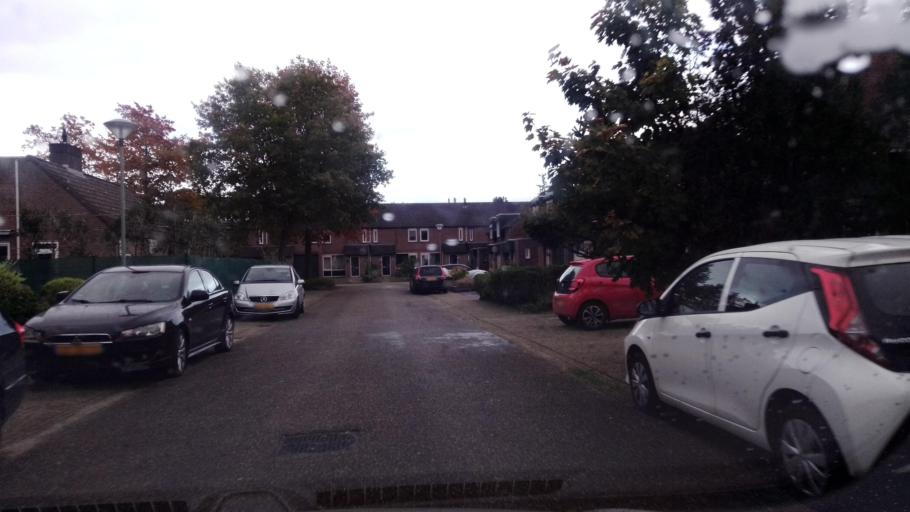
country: NL
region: Limburg
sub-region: Gemeente Venlo
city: Tegelen
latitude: 51.3306
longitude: 6.1498
